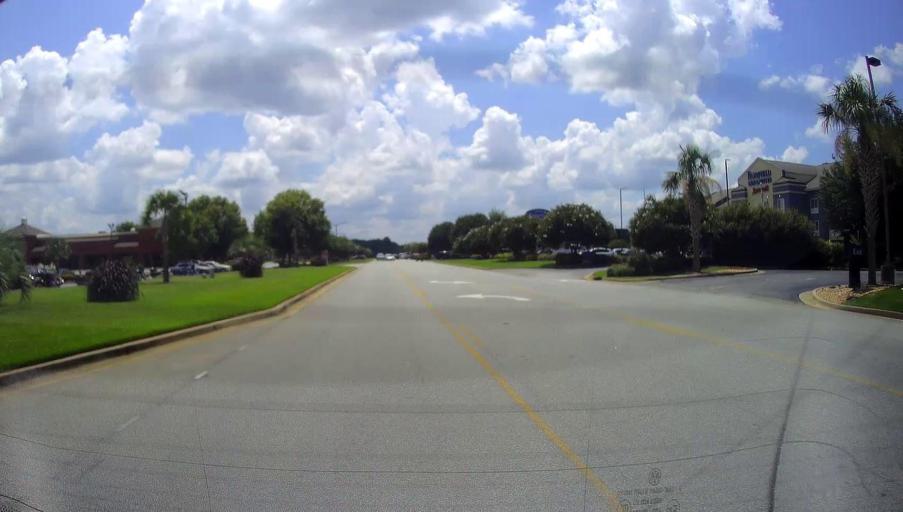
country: US
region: Georgia
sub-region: Houston County
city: Centerville
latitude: 32.6156
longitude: -83.6898
